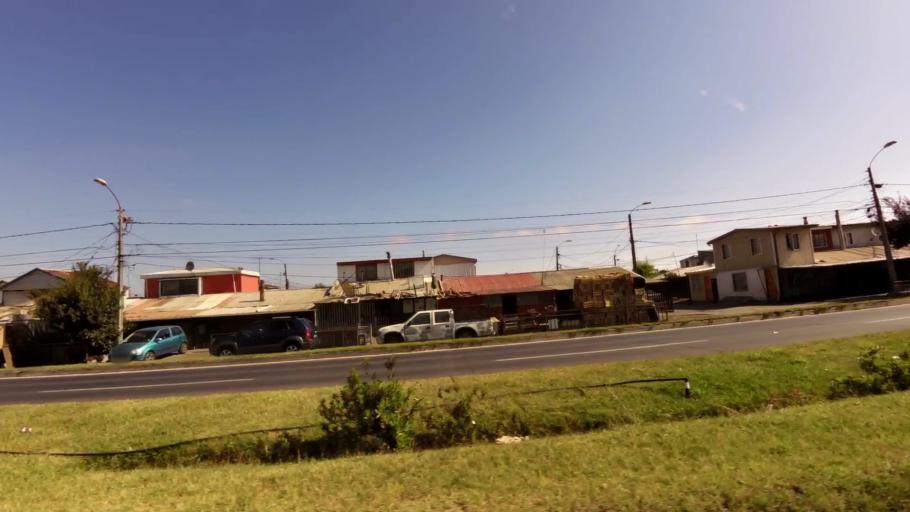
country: CL
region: Biobio
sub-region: Provincia de Concepcion
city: Talcahuano
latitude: -36.7775
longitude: -73.1078
